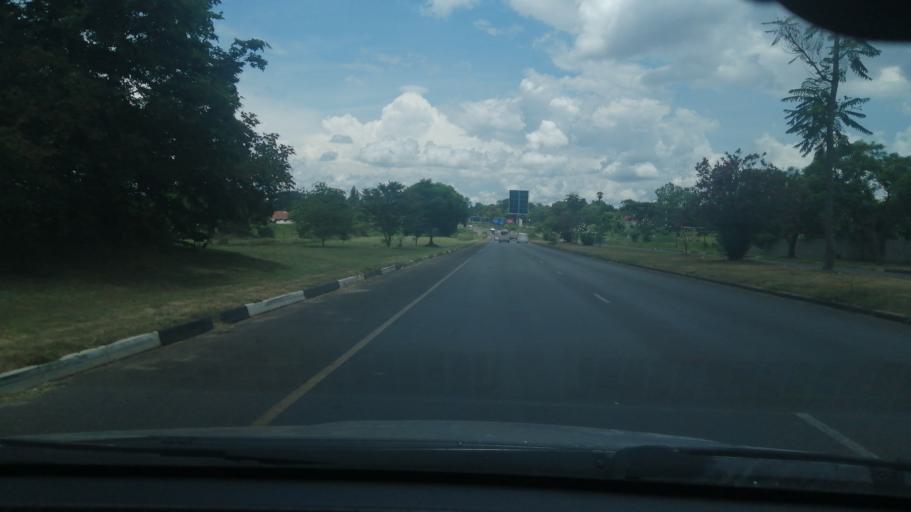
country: ZW
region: Harare
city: Harare
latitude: -17.8311
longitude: 31.1011
